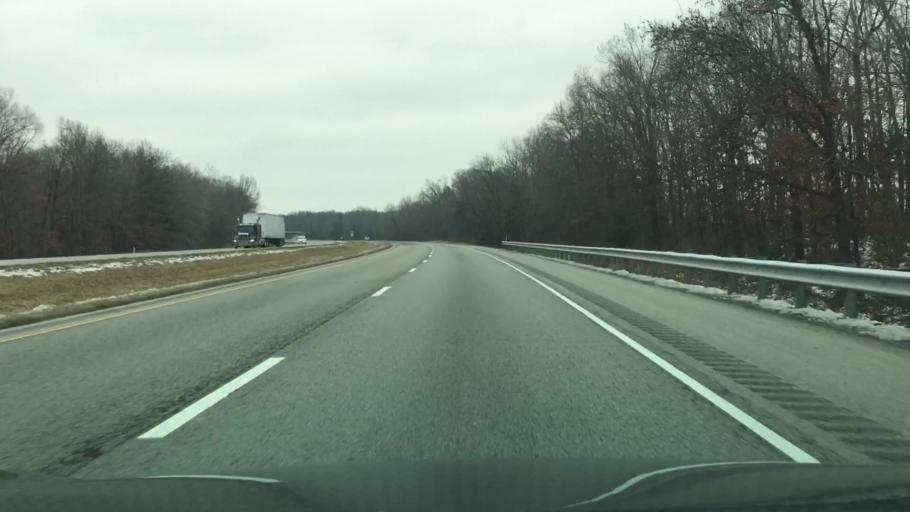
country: US
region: Illinois
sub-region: Franklin County
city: West Frankfort
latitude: 37.9440
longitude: -88.9377
